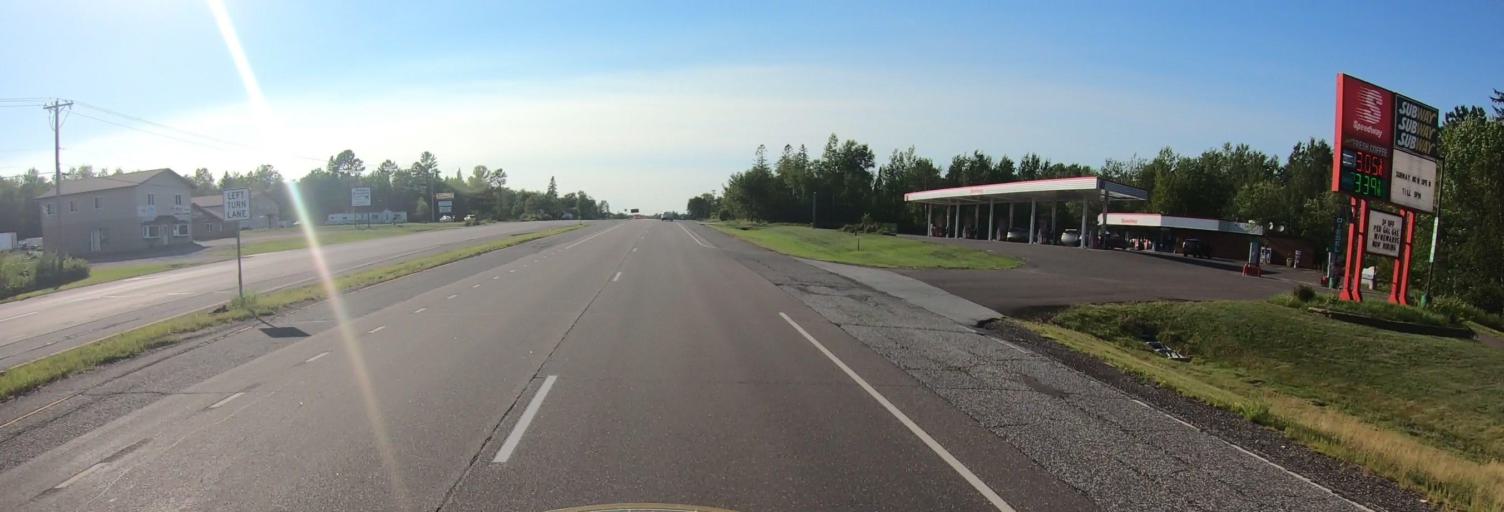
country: US
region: Minnesota
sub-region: Saint Louis County
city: Hermantown
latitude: 46.8479
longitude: -92.2711
